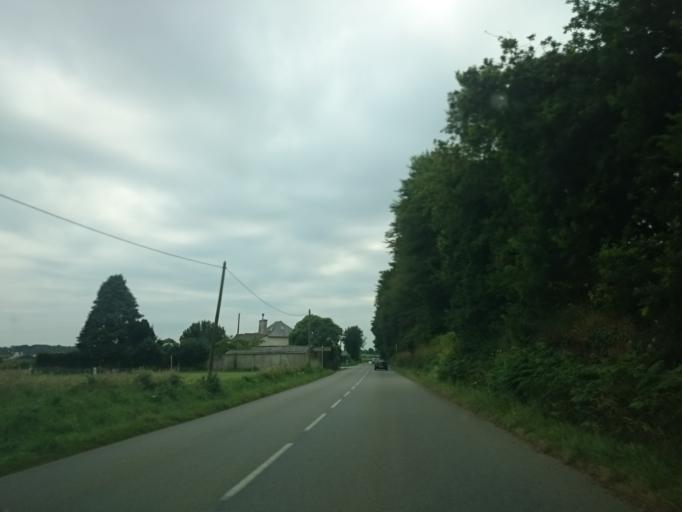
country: FR
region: Brittany
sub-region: Departement du Finistere
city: Ploumoguer
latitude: 48.4019
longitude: -4.6662
